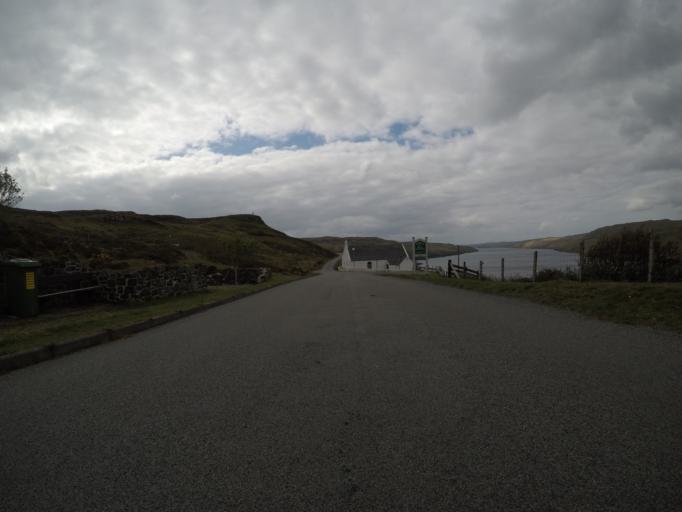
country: GB
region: Scotland
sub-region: Highland
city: Isle of Skye
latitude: 57.2960
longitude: -6.3399
